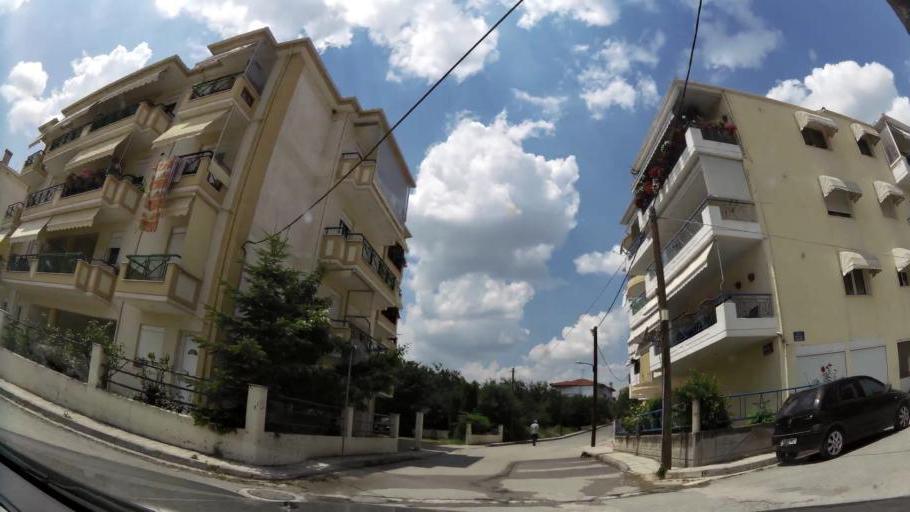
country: GR
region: West Macedonia
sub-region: Nomos Kozanis
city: Kozani
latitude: 40.2894
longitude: 21.7897
